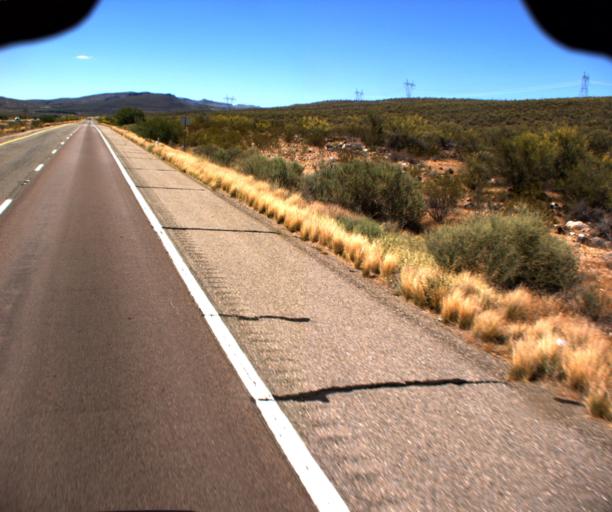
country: US
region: Arizona
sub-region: Yavapai County
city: Bagdad
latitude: 34.5178
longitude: -113.4208
